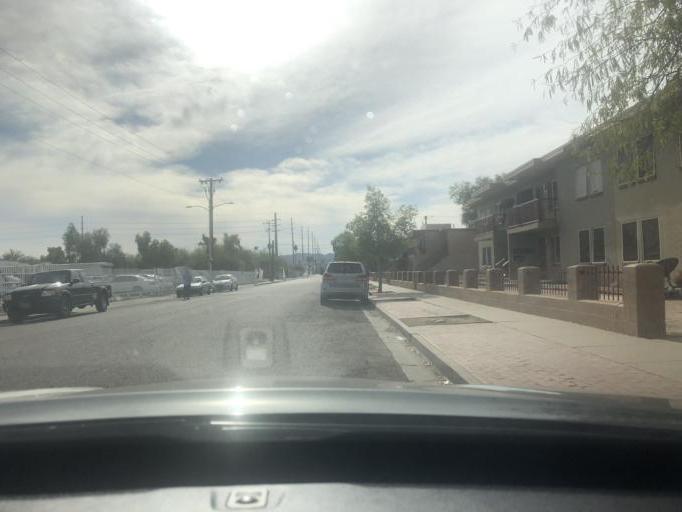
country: US
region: Arizona
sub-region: Maricopa County
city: Phoenix
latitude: 33.4510
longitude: -112.0434
